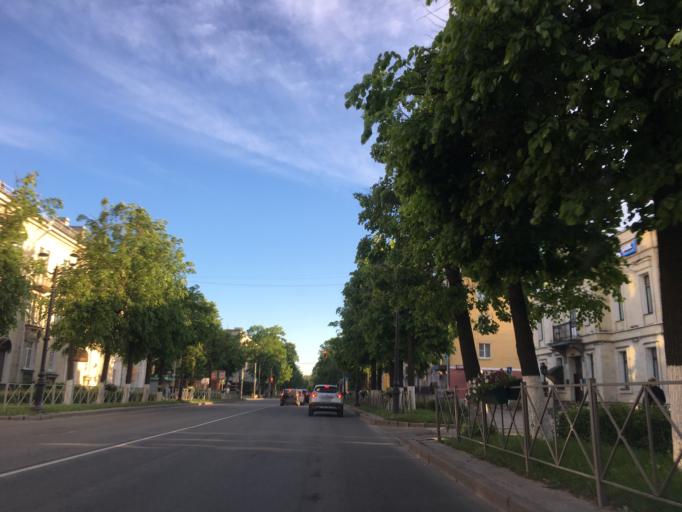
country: RU
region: Leningrad
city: Gatchina
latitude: 59.5734
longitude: 30.1264
